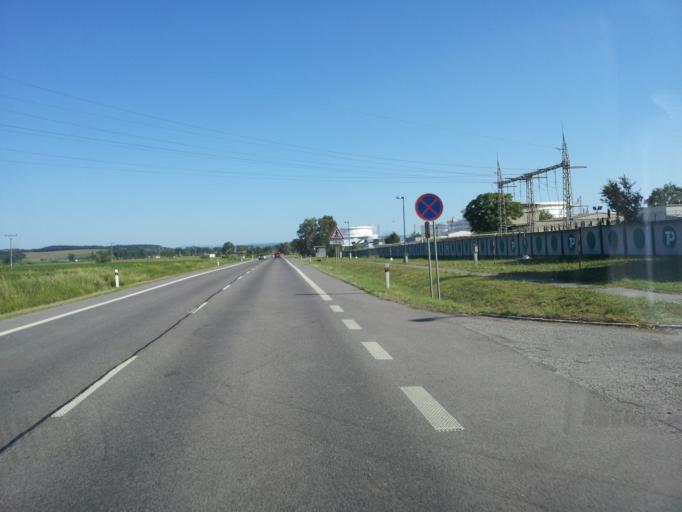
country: SK
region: Nitriansky
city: Sahy
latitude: 48.0975
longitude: 18.8940
